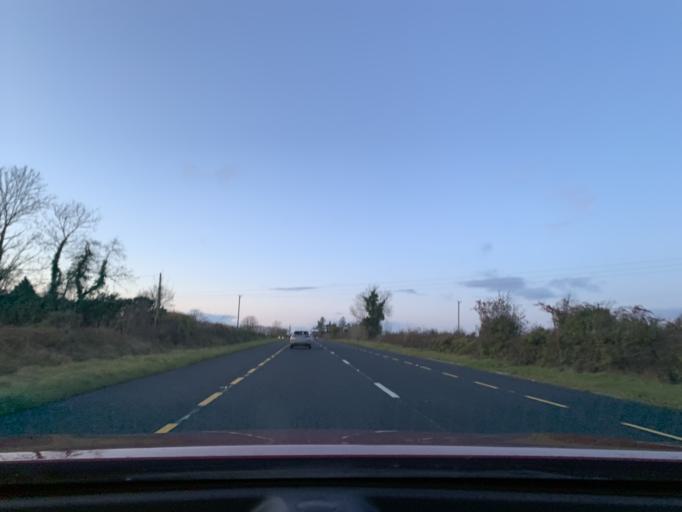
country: IE
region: Connaught
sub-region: County Leitrim
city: Carrick-on-Shannon
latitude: 53.8915
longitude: -7.9468
